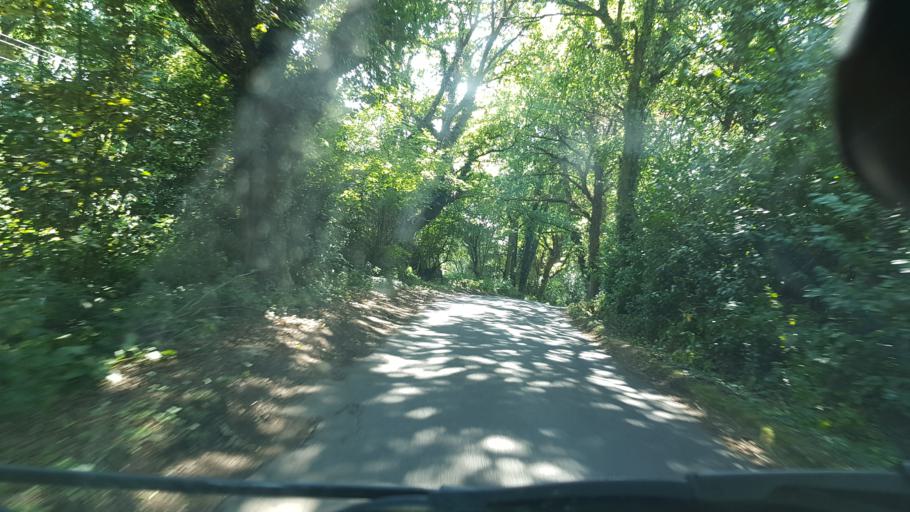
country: GB
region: England
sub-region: Surrey
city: Cranleigh
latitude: 51.1668
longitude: -0.4901
